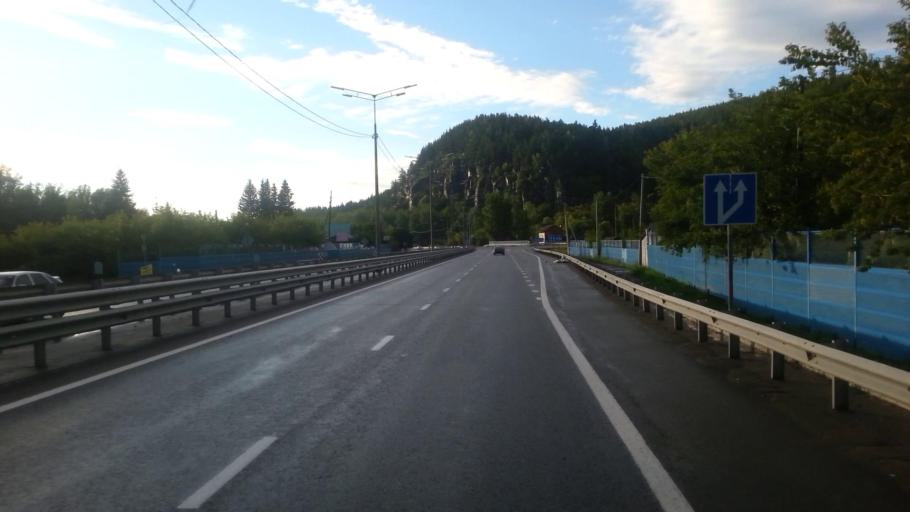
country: RU
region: Altay
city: Souzga
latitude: 51.9164
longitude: 85.8609
